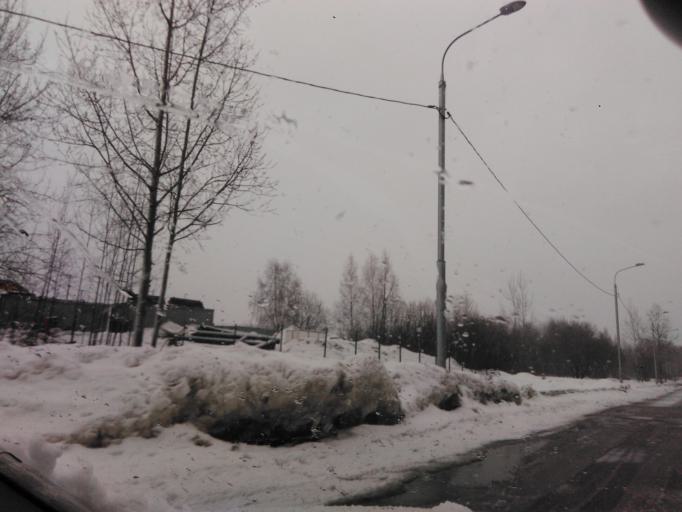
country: RU
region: Moskovskaya
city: Rzhavki
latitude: 56.0022
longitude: 37.2322
